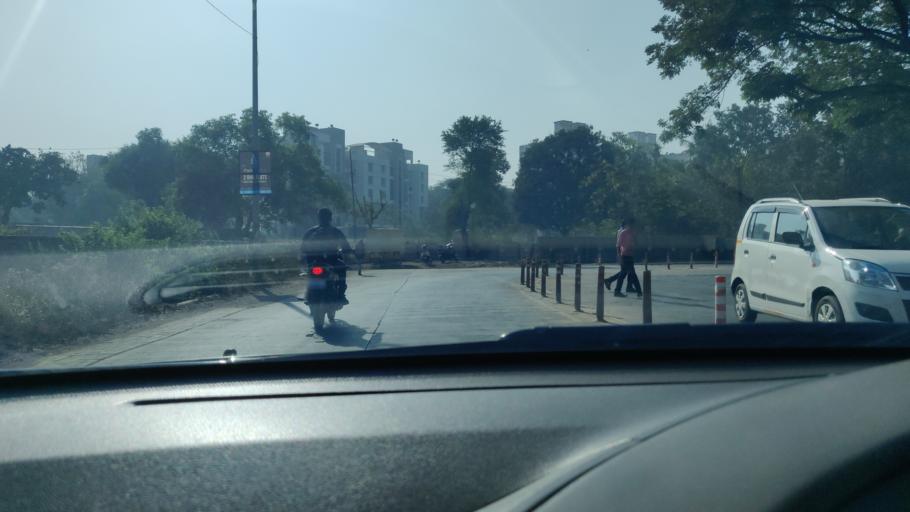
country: IN
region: Maharashtra
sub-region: Pune Division
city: Khadki
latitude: 18.5604
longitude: 73.7929
